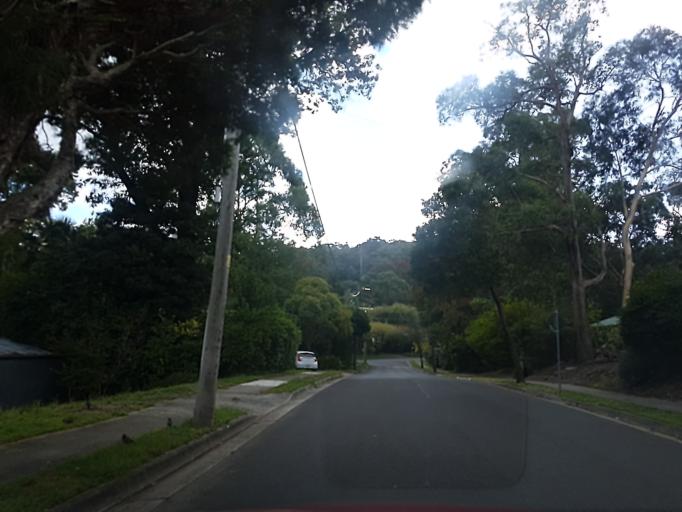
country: AU
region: Victoria
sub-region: Yarra Ranges
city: Tremont
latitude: -37.9003
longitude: 145.3332
